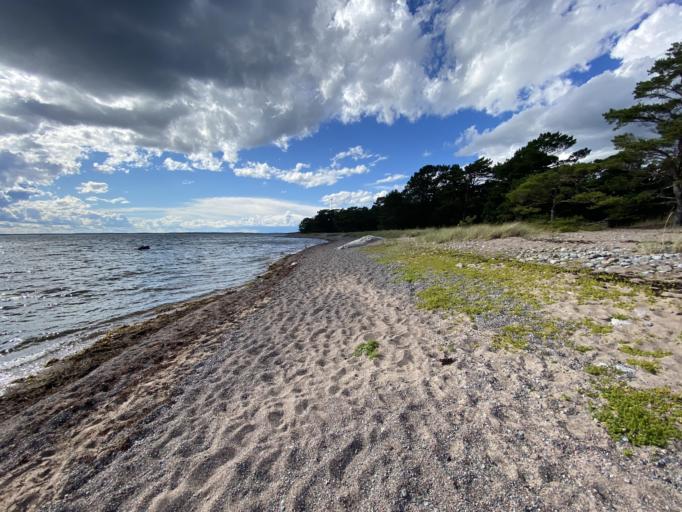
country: SE
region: Stockholm
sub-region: Varmdo Kommun
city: Holo
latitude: 59.2780
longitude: 18.9099
